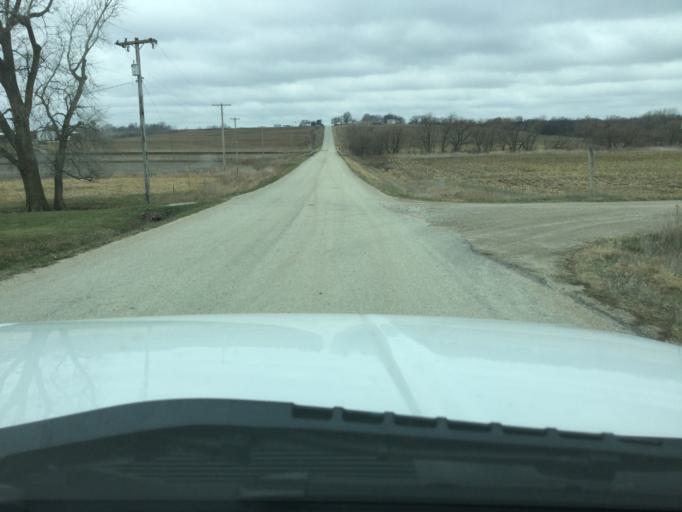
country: US
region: Kansas
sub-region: Nemaha County
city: Seneca
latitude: 39.7399
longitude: -96.0045
